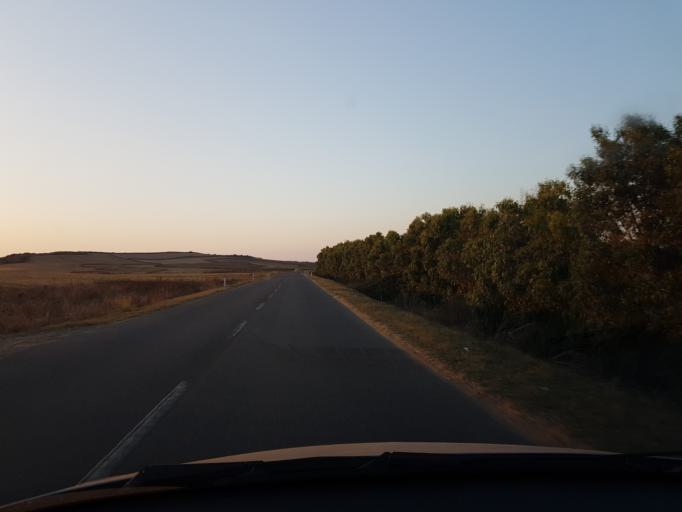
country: IT
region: Sardinia
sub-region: Provincia di Oristano
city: Nurachi
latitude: 39.9720
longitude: 8.4527
